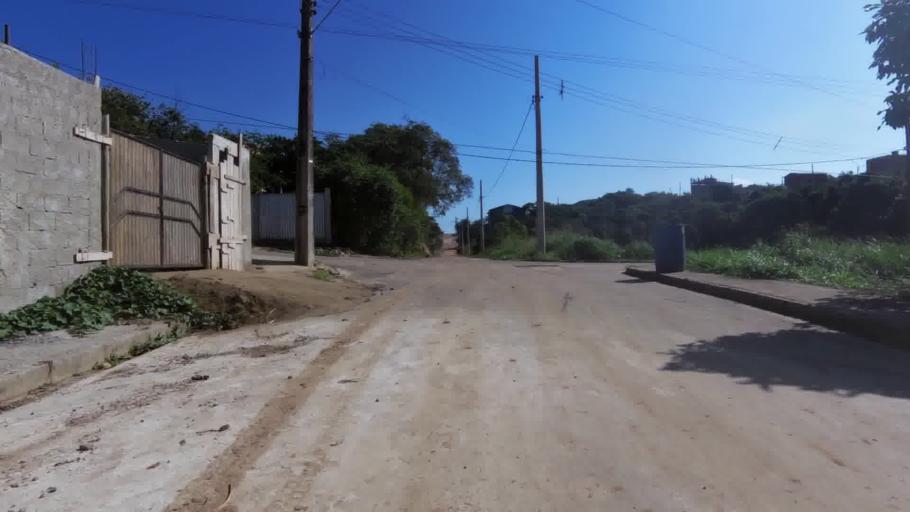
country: BR
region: Espirito Santo
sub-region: Piuma
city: Piuma
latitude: -20.8193
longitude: -40.6212
